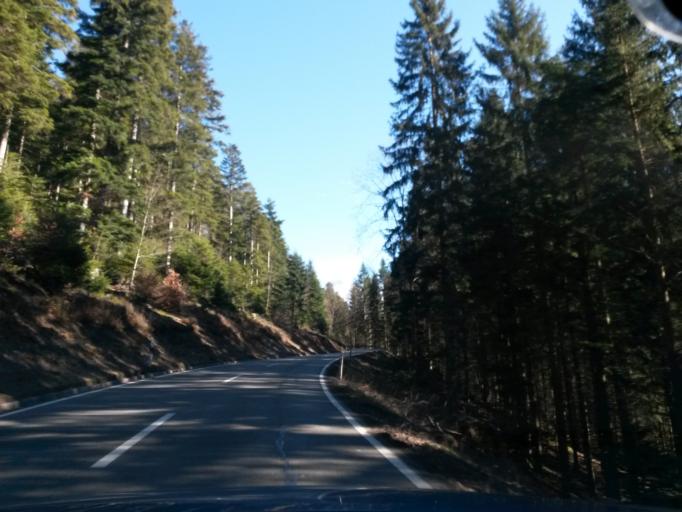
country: DE
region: Baden-Wuerttemberg
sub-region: Karlsruhe Region
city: Hofen an der Enz
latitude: 48.8017
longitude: 8.6001
